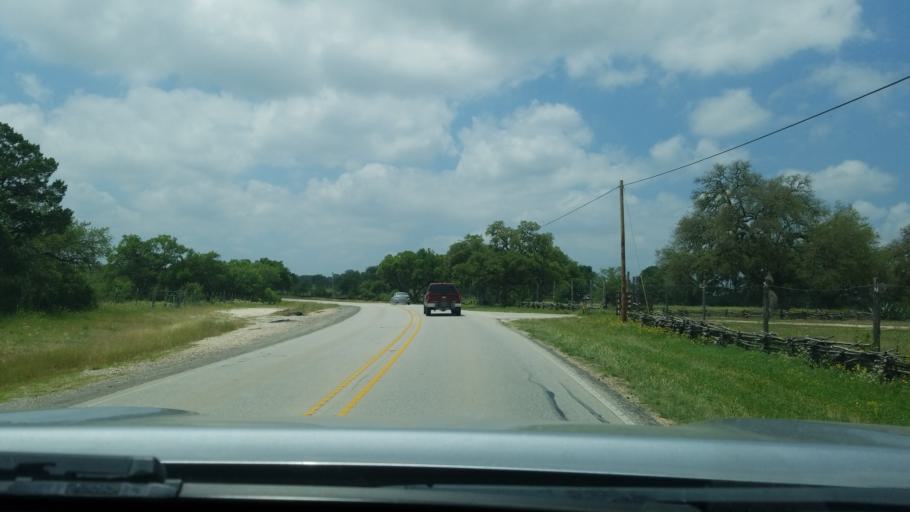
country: US
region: Texas
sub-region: Hays County
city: Dripping Springs
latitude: 30.1324
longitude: -98.0200
